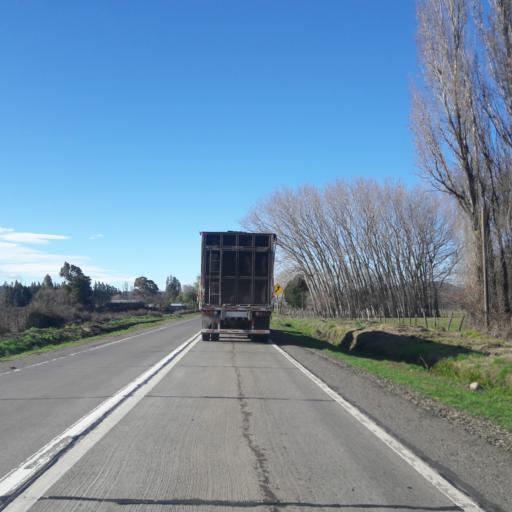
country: CL
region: Araucania
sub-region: Provincia de Malleco
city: Angol
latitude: -37.7825
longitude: -72.5306
